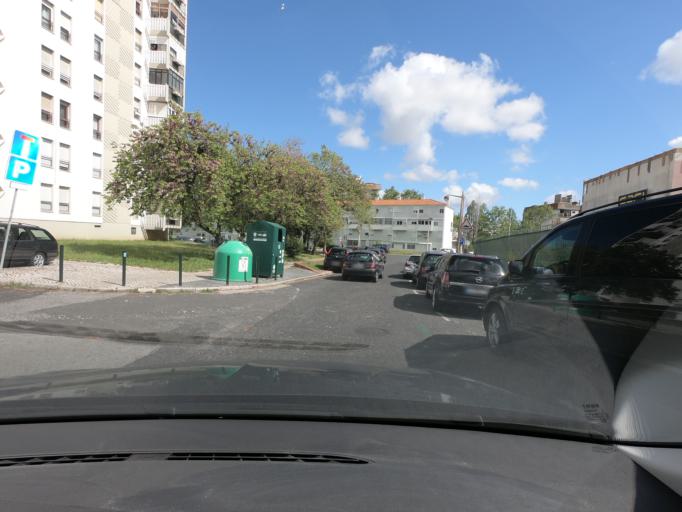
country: PT
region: Lisbon
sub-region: Loures
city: Moscavide
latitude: 38.7763
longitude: -9.1169
